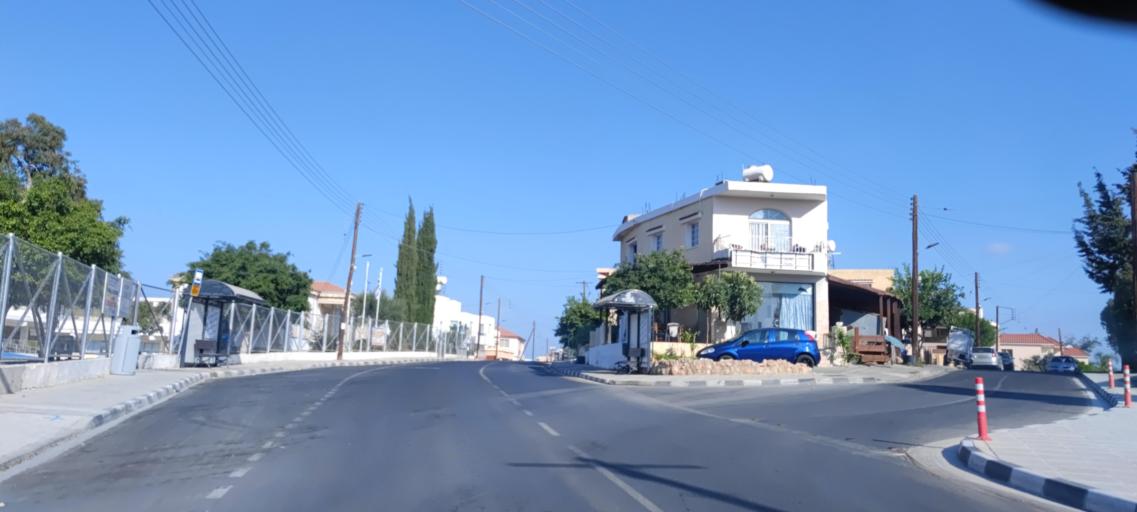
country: CY
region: Pafos
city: Chlorakas
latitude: 34.7942
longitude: 32.4121
